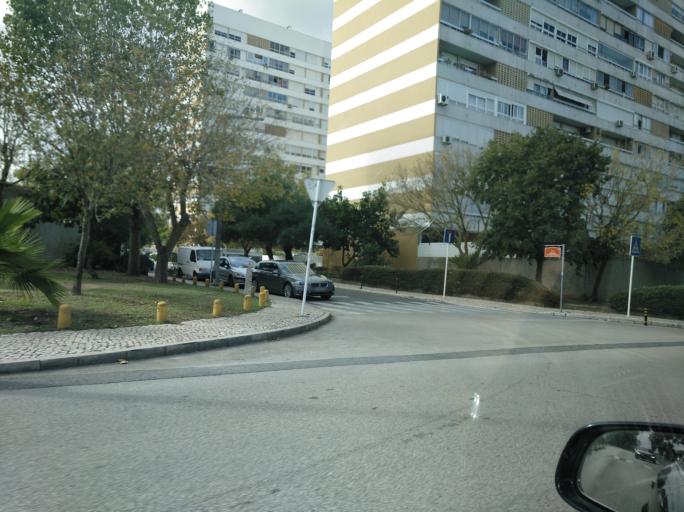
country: PT
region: Lisbon
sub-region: Loures
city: Moscavide
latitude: 38.7798
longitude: -9.1109
